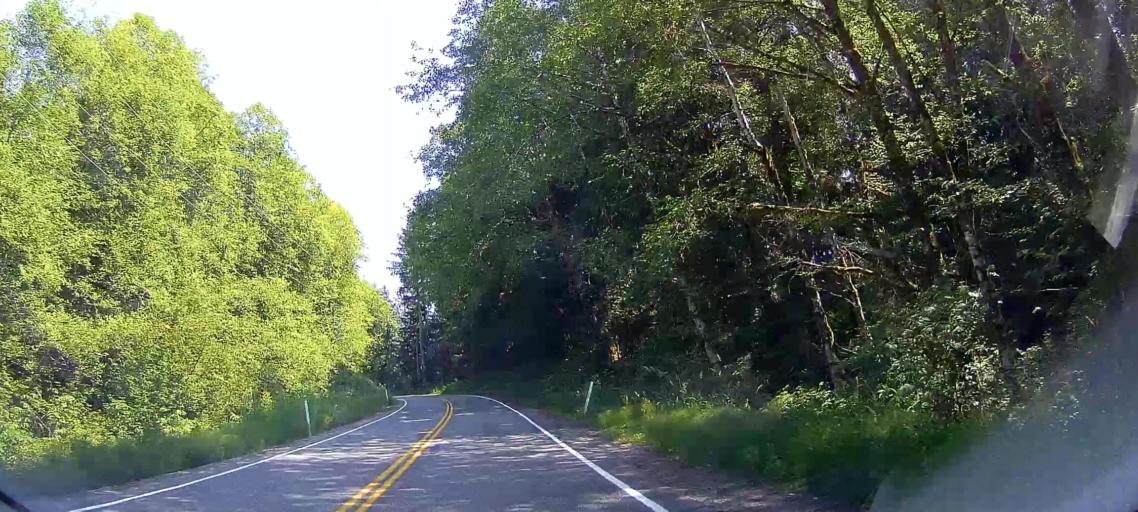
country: US
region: Washington
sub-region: Snohomish County
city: Bryant
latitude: 48.3442
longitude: -122.0662
